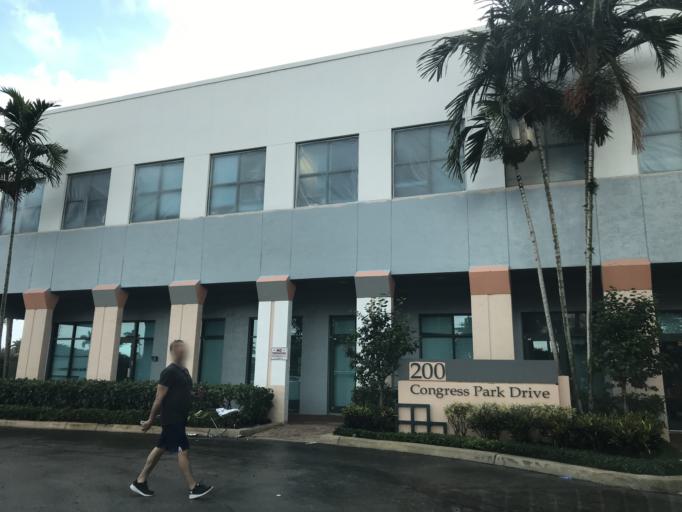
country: US
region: Florida
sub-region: Palm Beach County
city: Delray Beach
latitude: 26.4565
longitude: -80.0956
